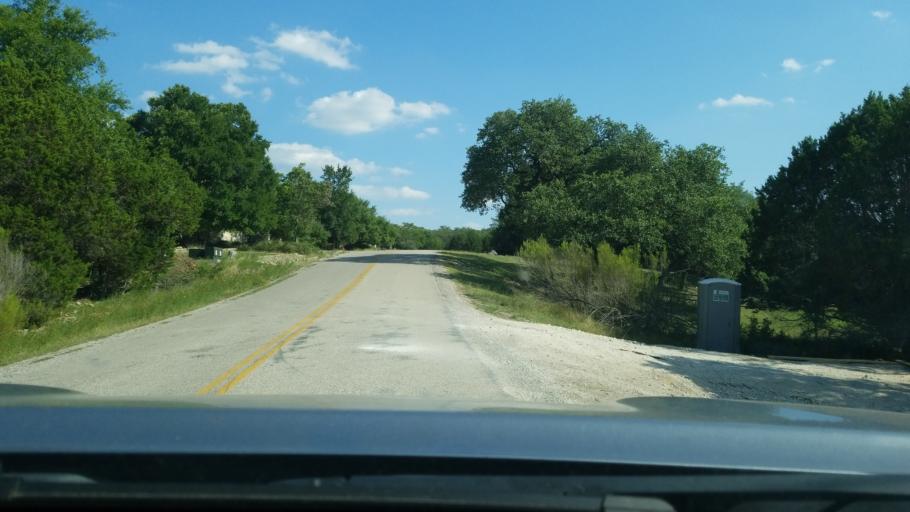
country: US
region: Texas
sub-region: Comal County
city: Bulverde
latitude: 29.8194
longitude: -98.4001
